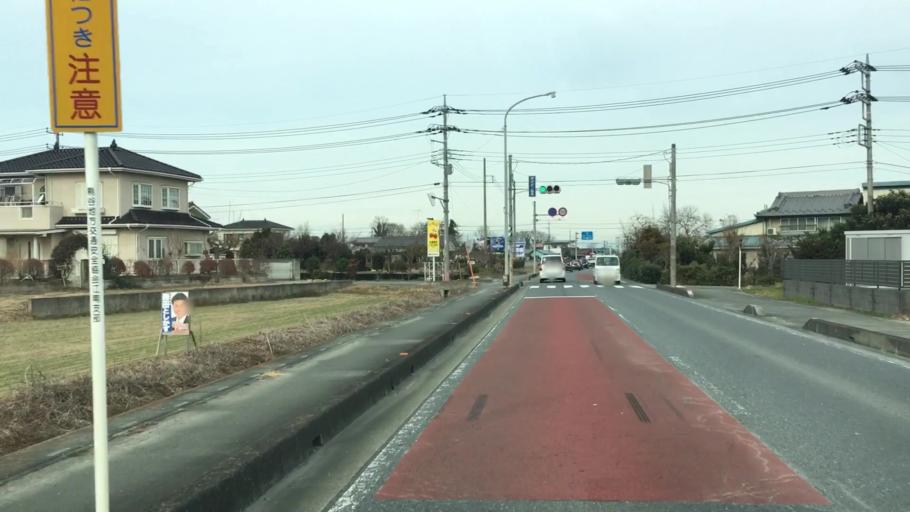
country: JP
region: Saitama
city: Kumagaya
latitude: 36.1288
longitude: 139.3241
